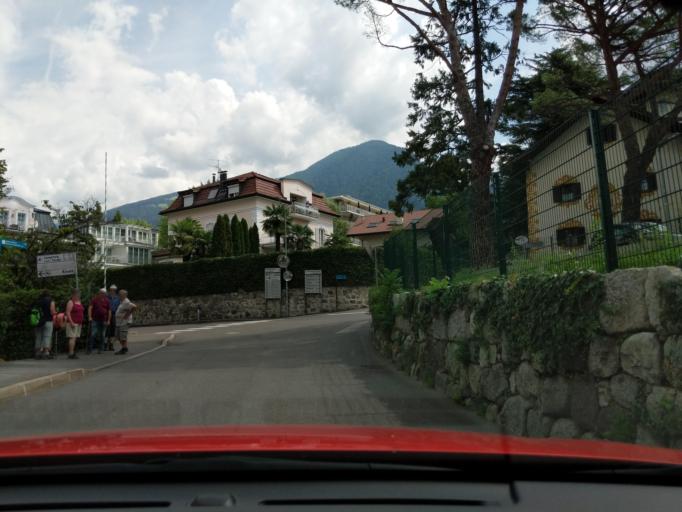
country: IT
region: Trentino-Alto Adige
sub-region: Bolzano
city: Merano
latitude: 46.6726
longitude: 11.1745
